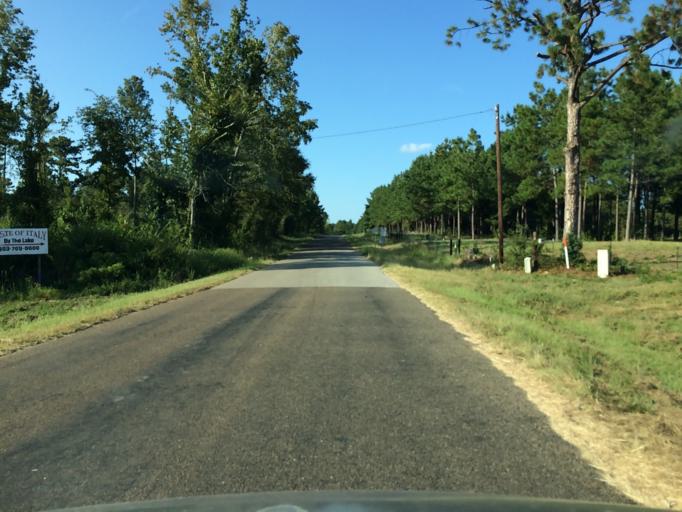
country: US
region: Texas
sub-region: Wood County
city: Hawkins
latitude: 32.5986
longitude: -95.2583
